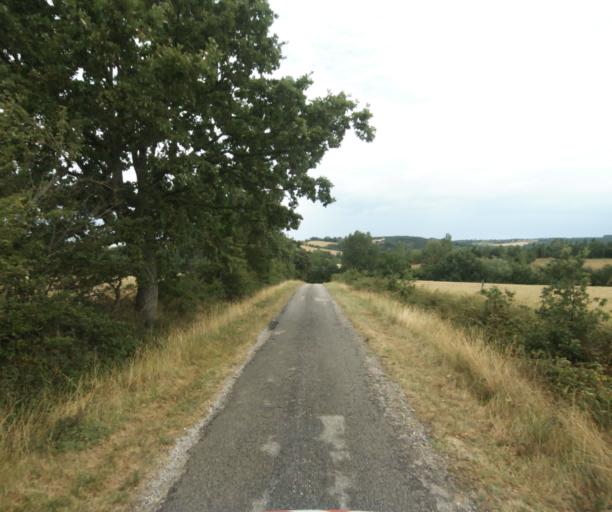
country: FR
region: Midi-Pyrenees
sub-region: Departement de la Haute-Garonne
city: Revel
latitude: 43.4196
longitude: 1.9779
